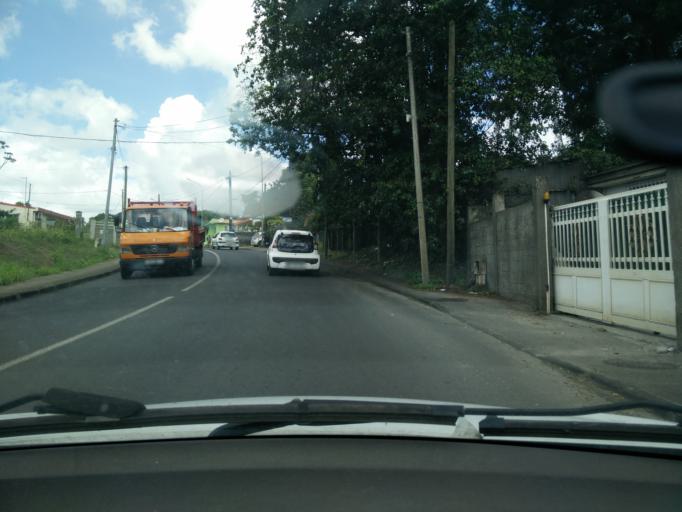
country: GP
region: Guadeloupe
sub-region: Guadeloupe
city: Les Abymes
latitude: 16.2615
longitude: -61.4986
